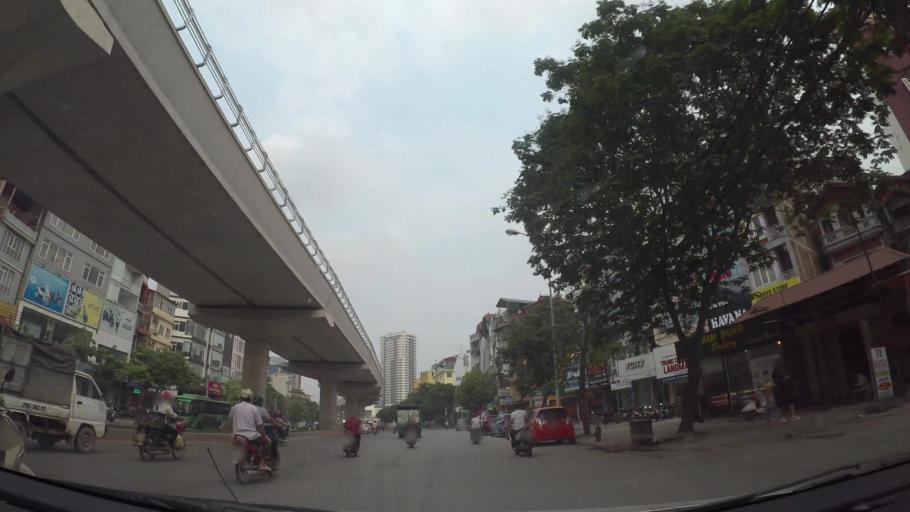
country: VN
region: Ha Noi
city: Cau Dien
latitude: 21.0367
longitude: 105.7770
